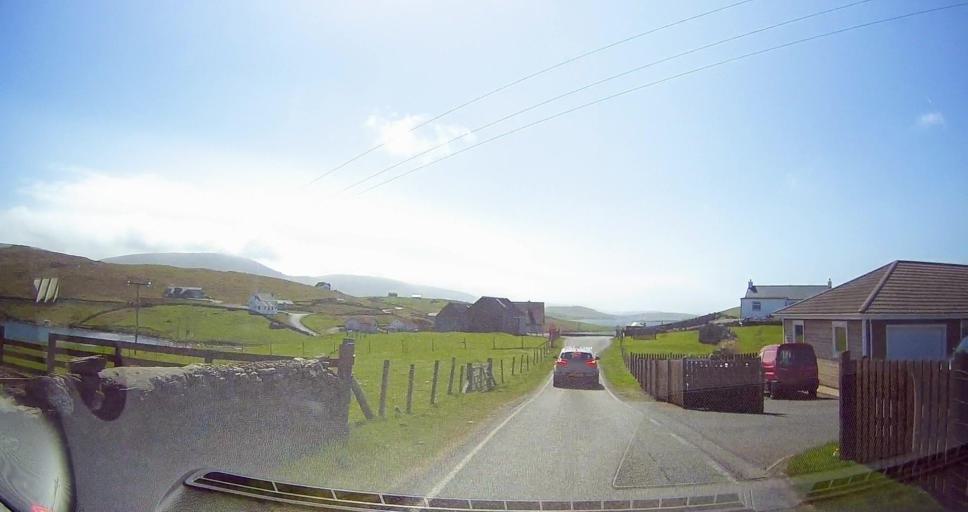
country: GB
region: Scotland
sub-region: Shetland Islands
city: Sandwick
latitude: 60.0841
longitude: -1.3324
